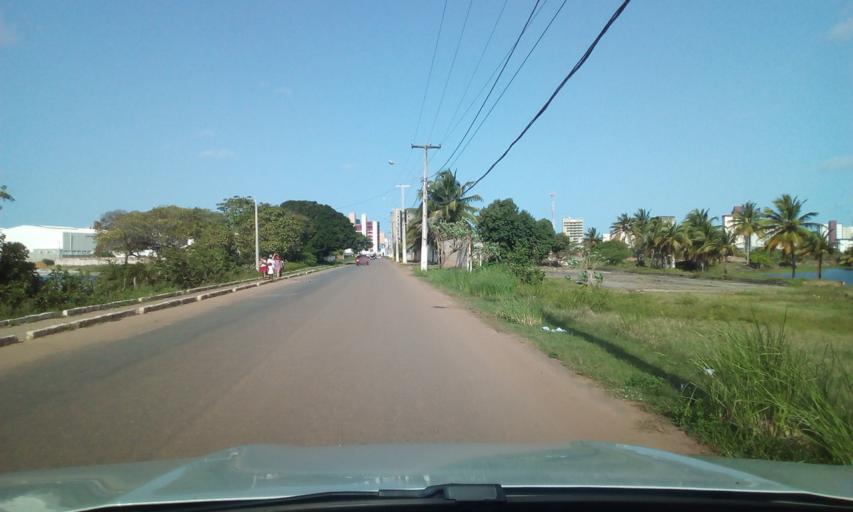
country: BR
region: Paraiba
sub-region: Cabedelo
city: Cabedelo
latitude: -7.0406
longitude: -34.8504
